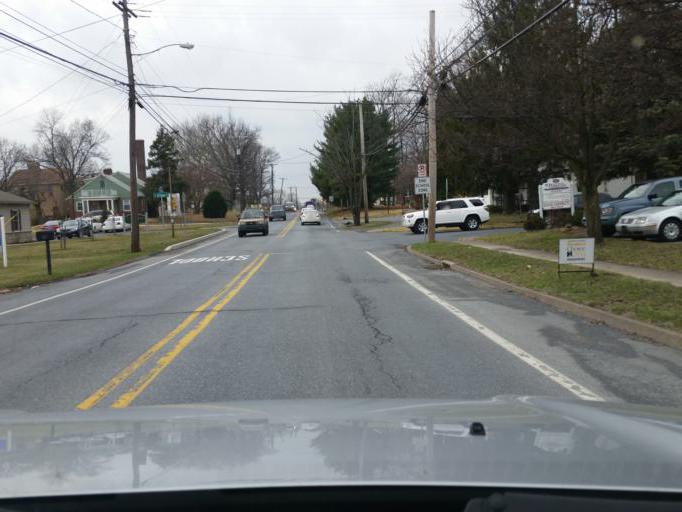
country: US
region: Pennsylvania
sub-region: Dauphin County
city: Paxtonia
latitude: 40.3201
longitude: -76.7842
